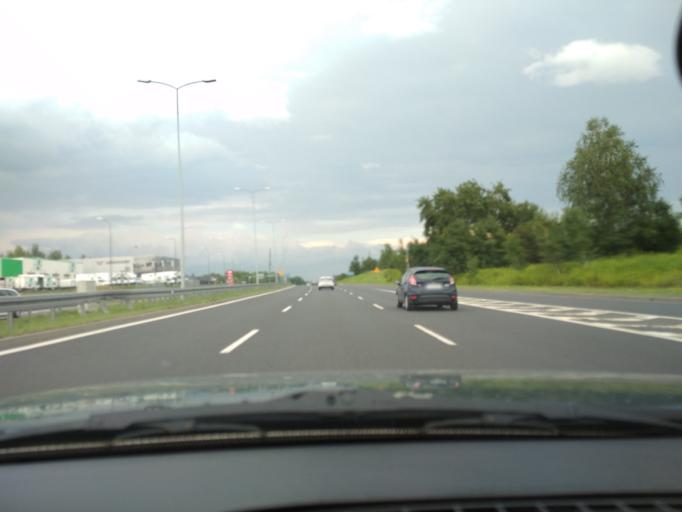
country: PL
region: Silesian Voivodeship
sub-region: Ruda Slaska
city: Ruda Slaska
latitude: 50.2992
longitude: 18.8622
